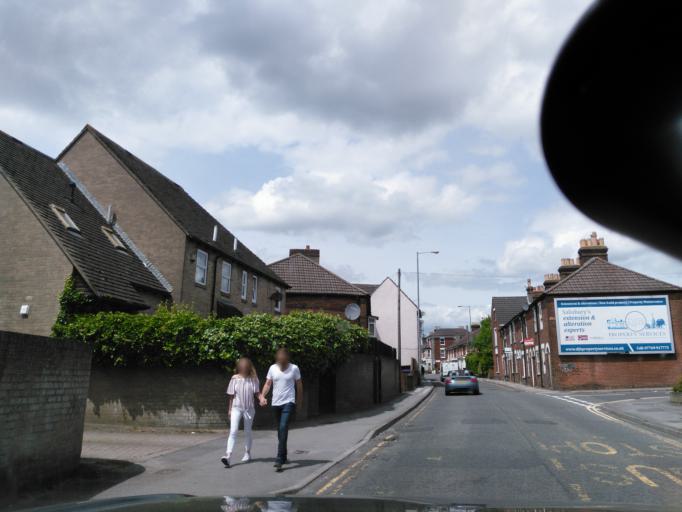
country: GB
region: England
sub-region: Wiltshire
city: Salisbury
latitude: 51.0733
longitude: -1.8060
